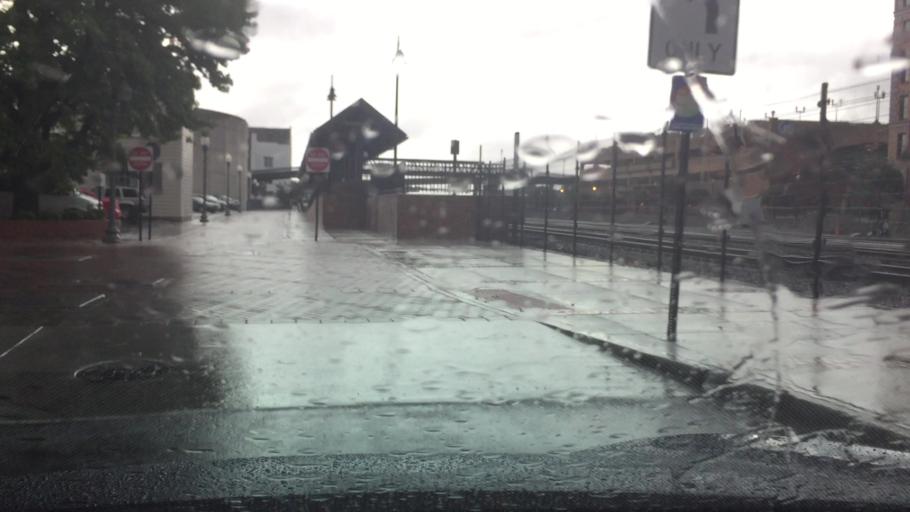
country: US
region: Virginia
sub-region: City of Roanoke
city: Roanoke
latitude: 37.2731
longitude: -79.9403
